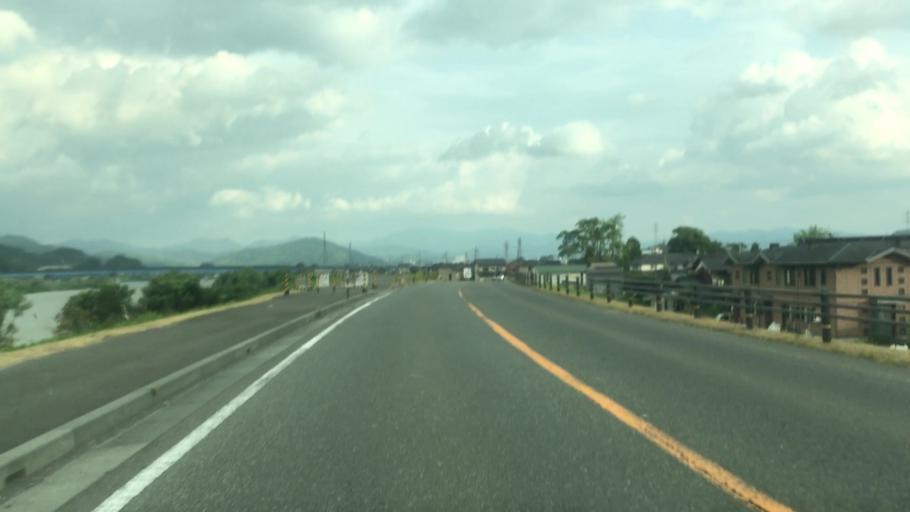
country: JP
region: Hyogo
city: Toyooka
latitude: 35.5615
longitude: 134.8139
